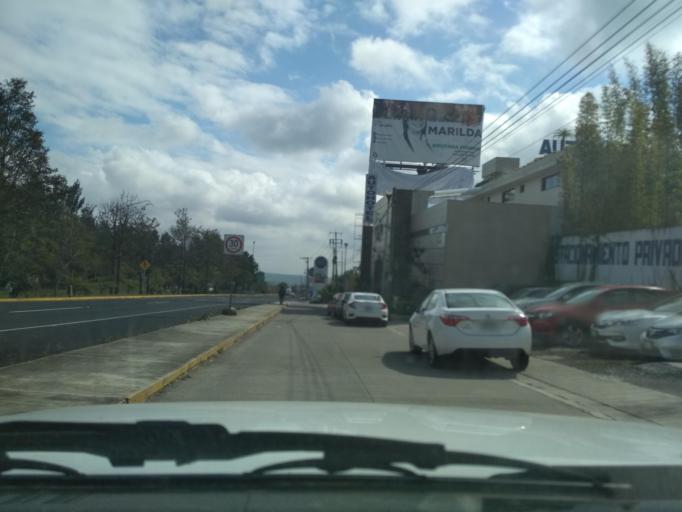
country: MX
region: Veracruz
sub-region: Emiliano Zapata
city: Jacarandas
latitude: 19.4993
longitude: -96.8397
